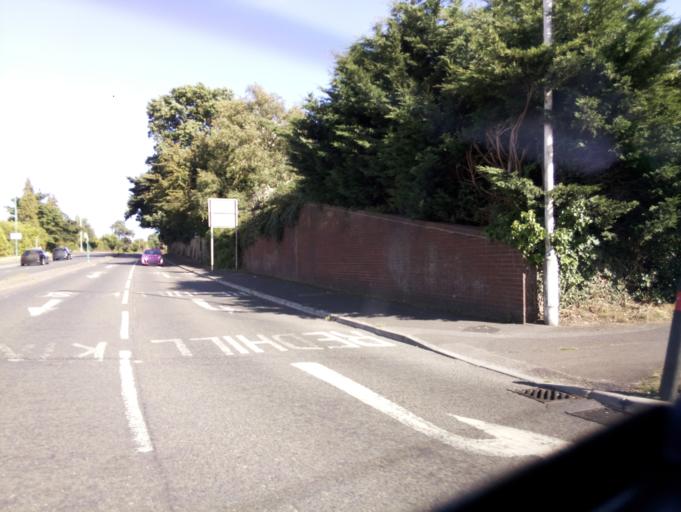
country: GB
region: England
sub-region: Bournemouth
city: Bournemouth
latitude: 50.7617
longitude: -1.8744
